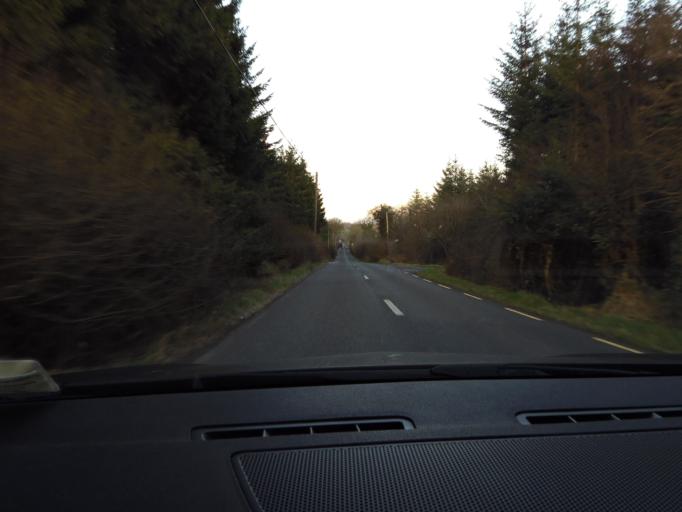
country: IE
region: Connaught
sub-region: Roscommon
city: Boyle
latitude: 53.9693
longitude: -8.3730
